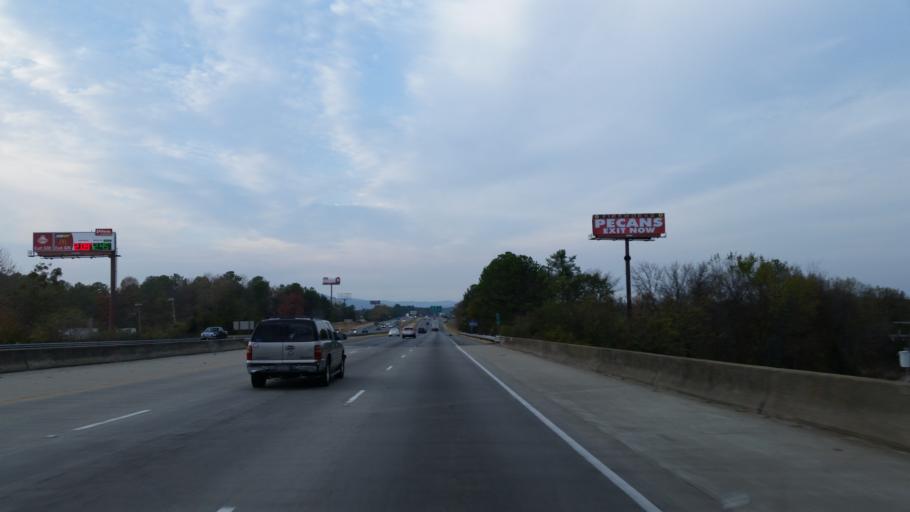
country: US
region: Georgia
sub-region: Gordon County
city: Calhoun
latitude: 34.5509
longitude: -84.9300
